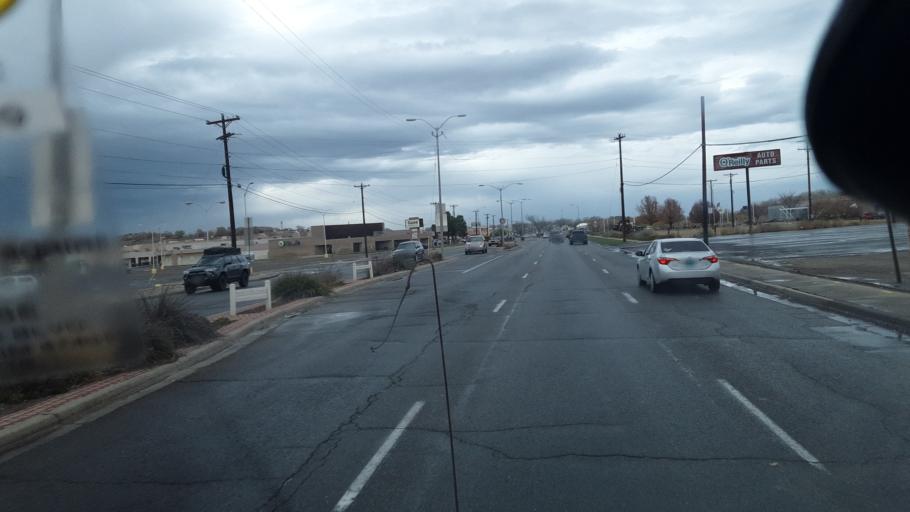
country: US
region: New Mexico
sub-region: San Juan County
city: Farmington
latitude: 36.7436
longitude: -108.1669
